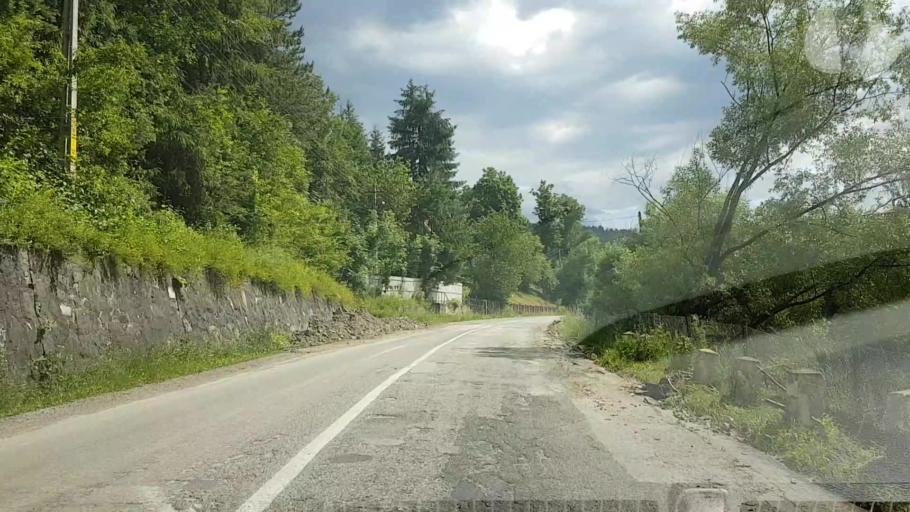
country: RO
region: Neamt
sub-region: Comuna Poiana Teiului
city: Poiana Teiului
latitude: 47.0871
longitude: 25.9705
